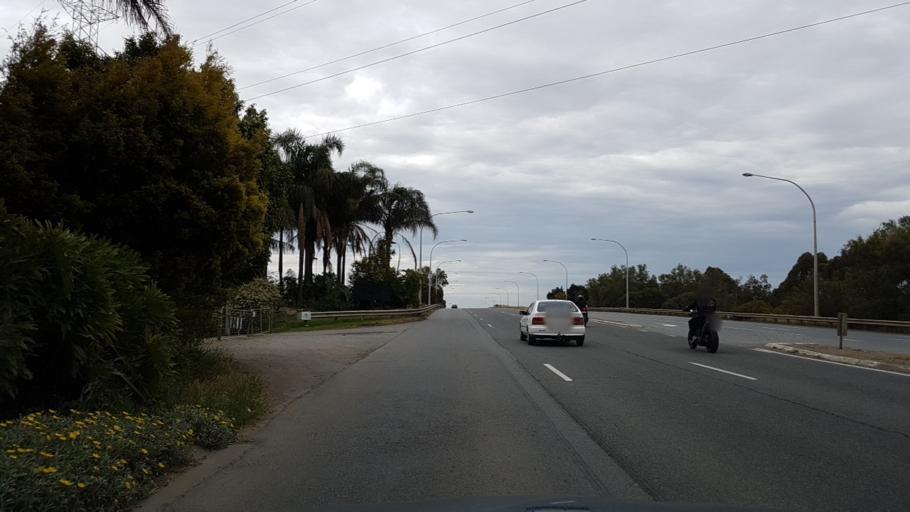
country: AU
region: South Australia
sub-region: Port Adelaide Enfield
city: Enfield
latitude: -34.8220
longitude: 138.5980
